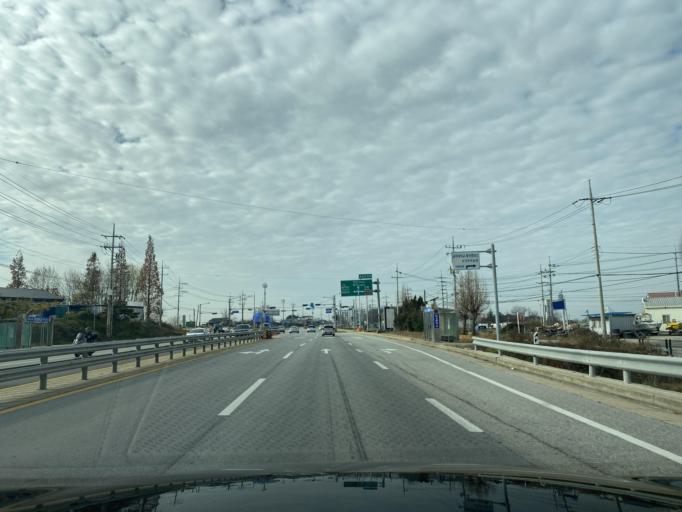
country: KR
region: Chungcheongnam-do
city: Yesan
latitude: 36.6877
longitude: 126.7853
